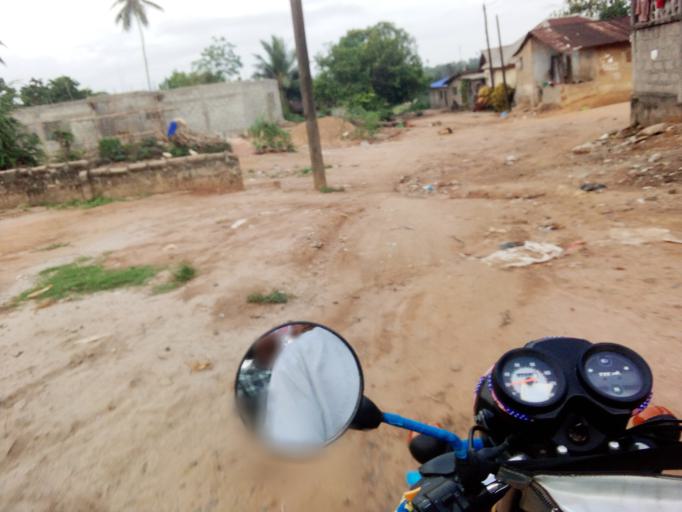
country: SL
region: Western Area
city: Waterloo
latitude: 8.3324
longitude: -13.0696
